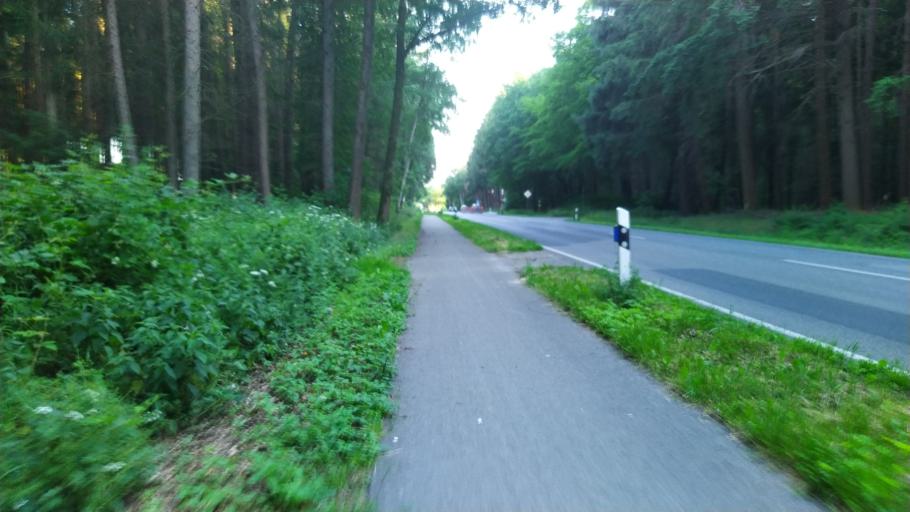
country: DE
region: Lower Saxony
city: Alfstedt
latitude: 53.5386
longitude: 9.0559
